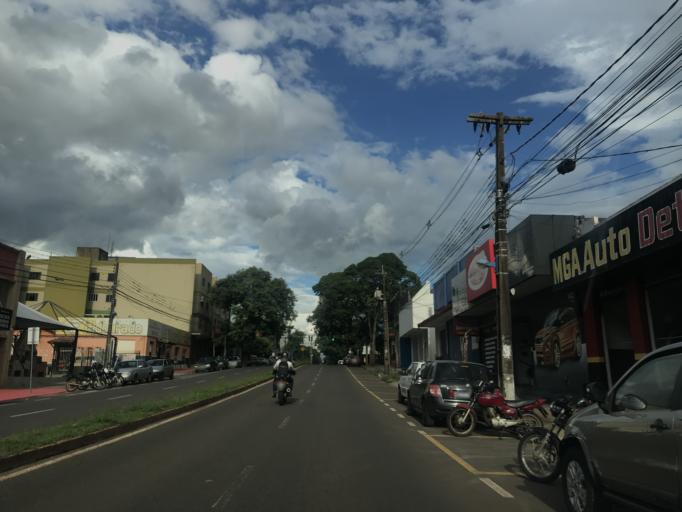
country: BR
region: Parana
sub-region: Maringa
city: Maringa
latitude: -23.4243
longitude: -51.9588
